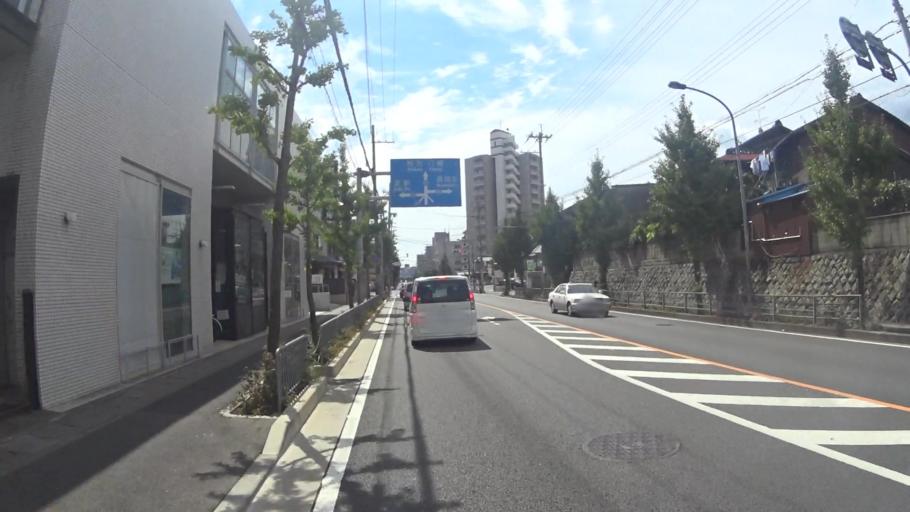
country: JP
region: Kyoto
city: Yawata
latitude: 34.9083
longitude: 135.7194
